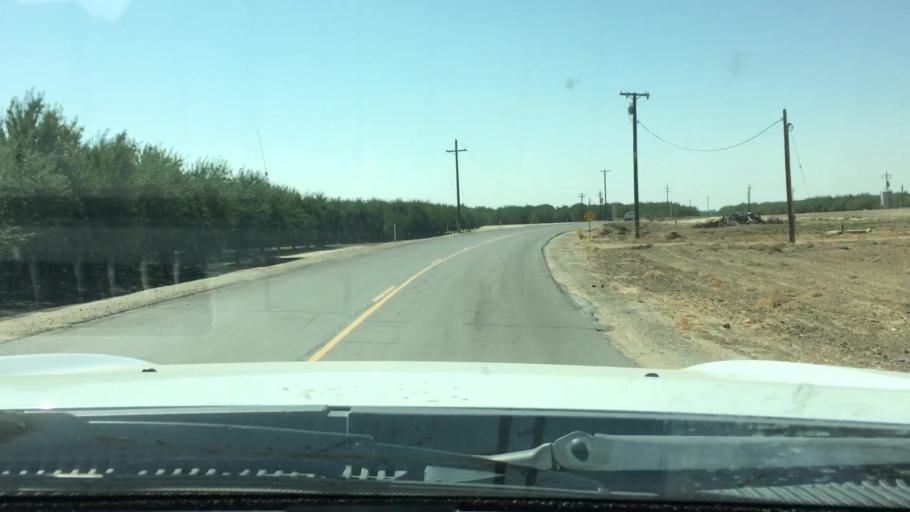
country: US
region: California
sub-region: Kern County
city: Shafter
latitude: 35.5518
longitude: -119.2767
